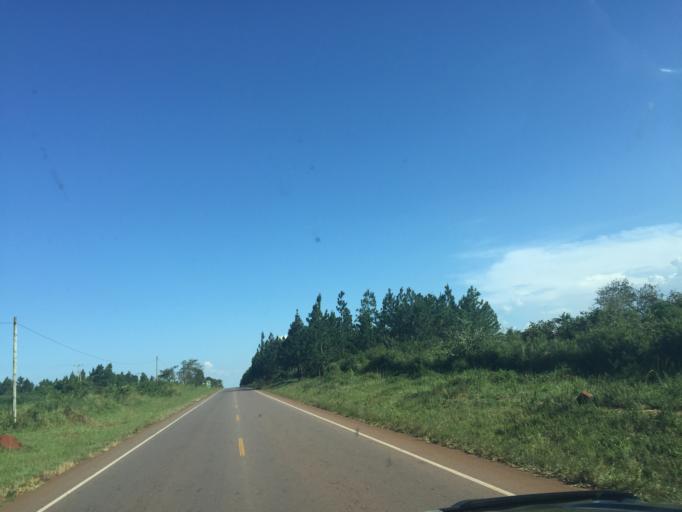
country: UG
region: Central Region
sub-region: Nakasongola District
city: Nakasongola
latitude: 1.3788
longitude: 32.3415
